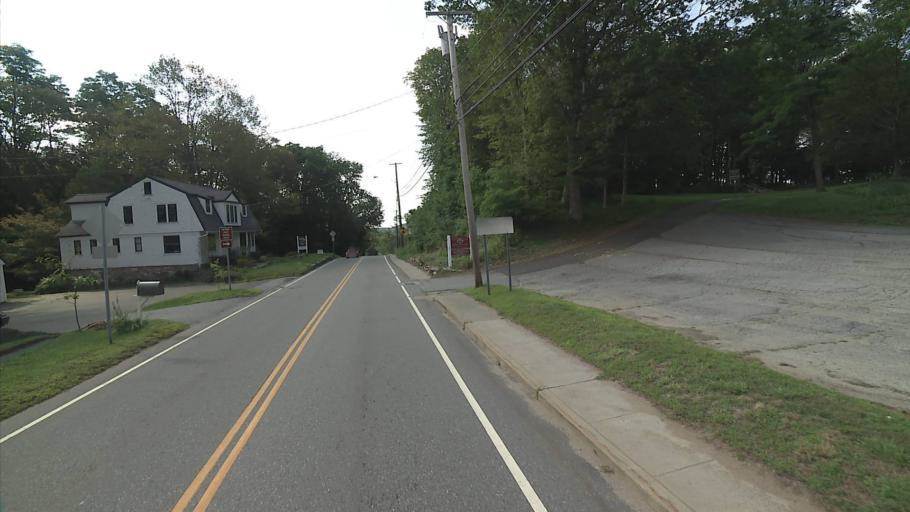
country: US
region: Connecticut
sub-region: Middlesex County
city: East Haddam
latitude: 41.4549
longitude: -72.4619
